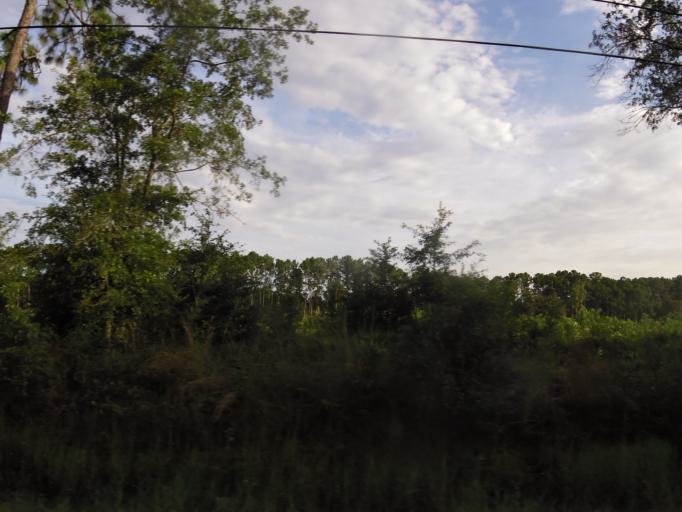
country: US
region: Florida
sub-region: Nassau County
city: Nassau Village-Ratliff
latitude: 30.4161
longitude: -81.7447
